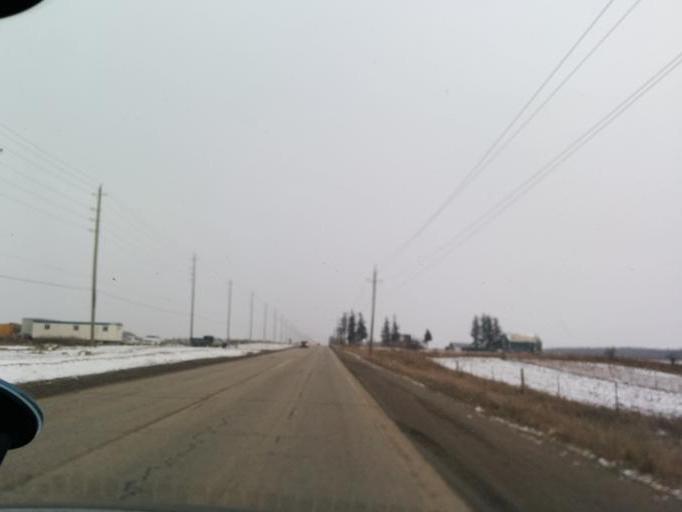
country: CA
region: Ontario
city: Brampton
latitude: 43.6914
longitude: -79.8628
